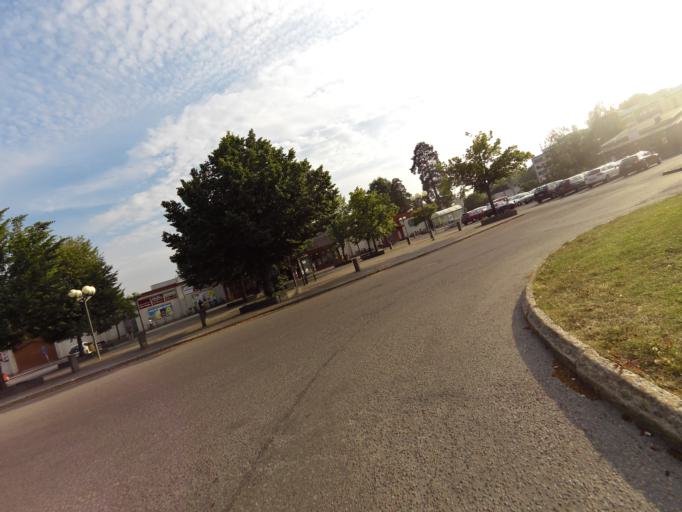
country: SE
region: Gaevleborg
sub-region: Gavle Kommun
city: Gavle
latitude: 60.6926
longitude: 17.1169
